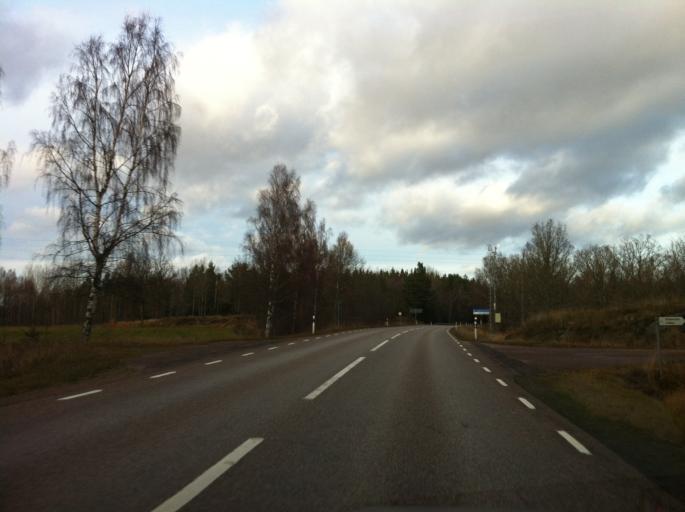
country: SE
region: Kronoberg
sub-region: Uppvidinge Kommun
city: Aseda
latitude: 57.1705
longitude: 15.4942
